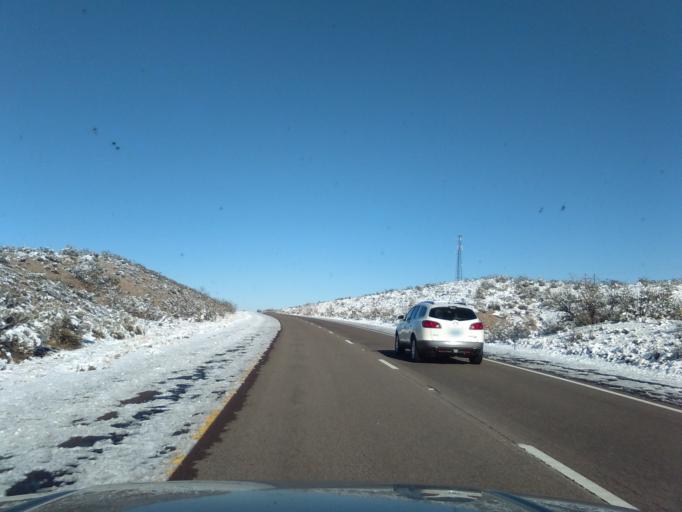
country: US
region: New Mexico
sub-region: Socorro County
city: Socorro
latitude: 33.6626
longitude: -107.0893
